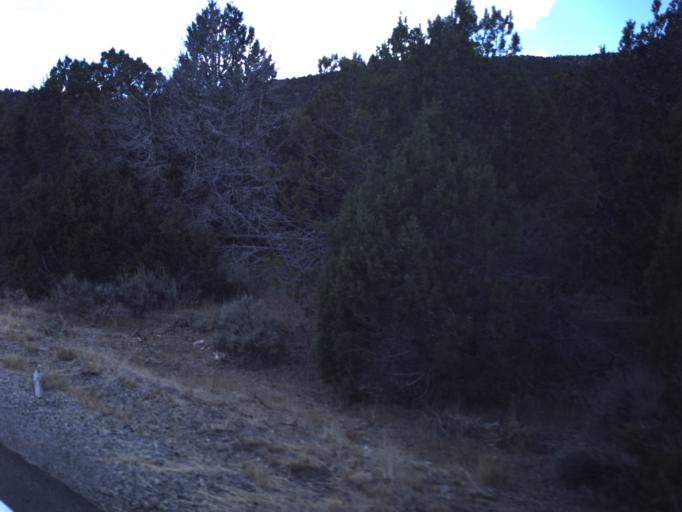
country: US
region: Utah
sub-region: Tooele County
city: Grantsville
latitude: 40.3472
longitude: -112.5616
